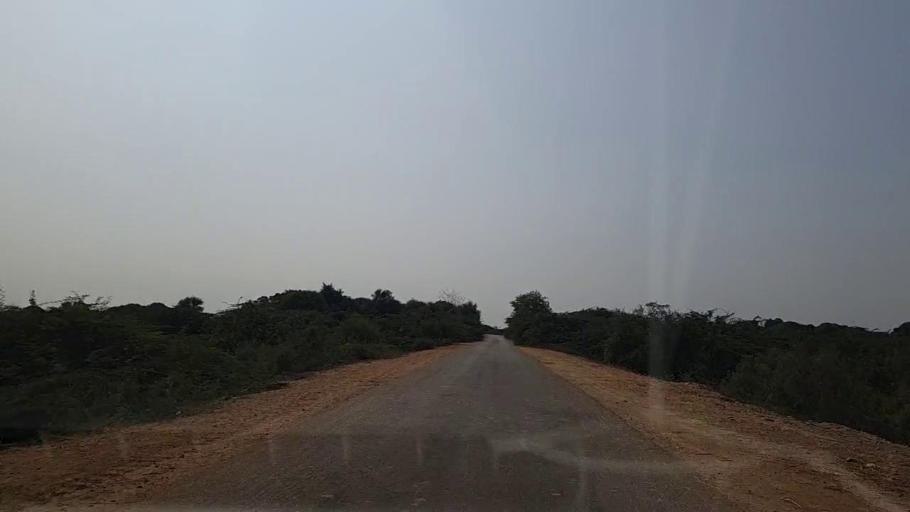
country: PK
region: Sindh
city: Chuhar Jamali
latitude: 24.2683
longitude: 67.9111
